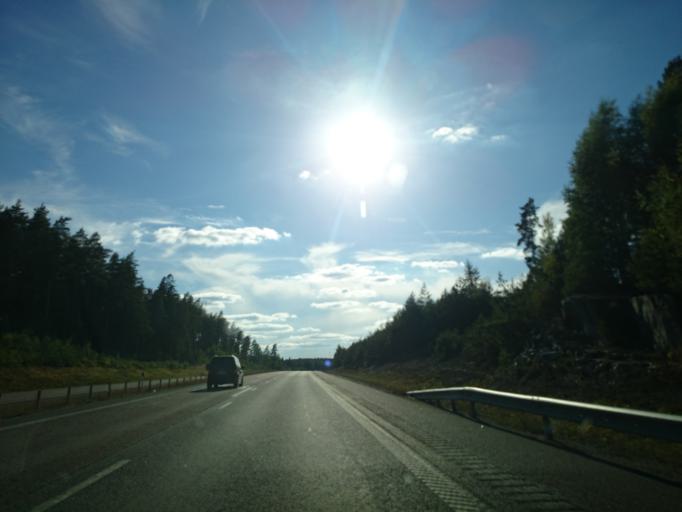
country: SE
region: Soedermanland
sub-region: Nykopings Kommun
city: Olstorp
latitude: 58.7546
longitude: 16.5965
